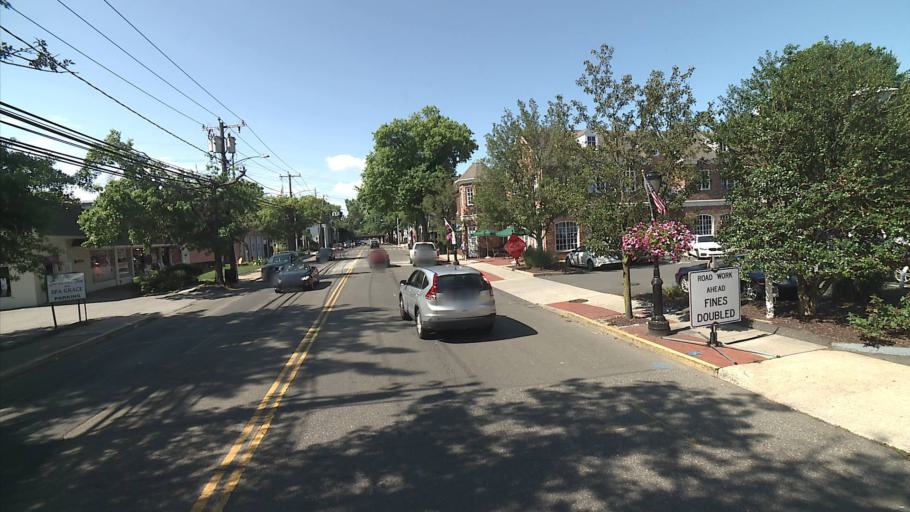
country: US
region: Connecticut
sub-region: Fairfield County
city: Darien
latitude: 41.0788
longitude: -73.4686
